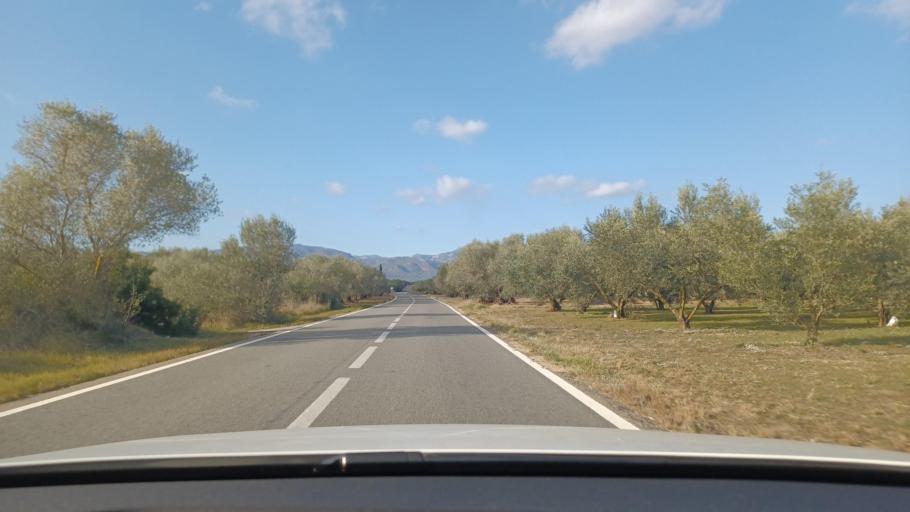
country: ES
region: Catalonia
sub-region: Provincia de Tarragona
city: Ulldecona
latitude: 40.6360
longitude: 0.3579
